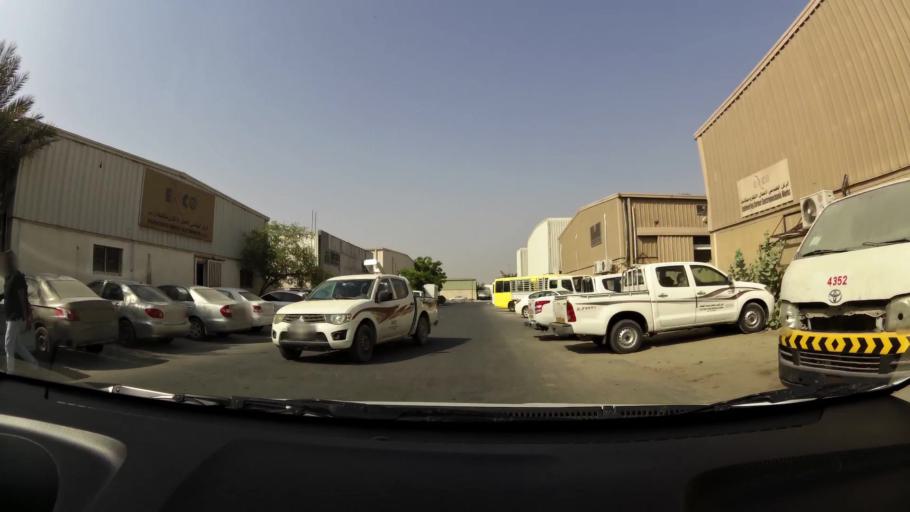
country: AE
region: Ash Shariqah
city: Sharjah
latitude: 25.2967
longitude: 55.3902
